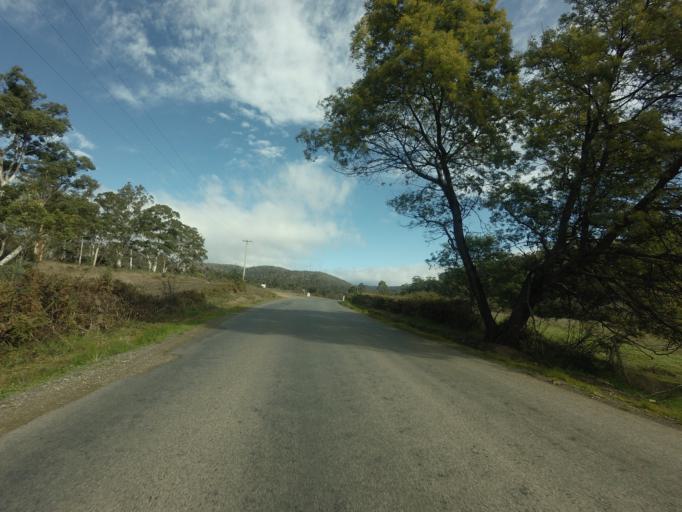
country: AU
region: Tasmania
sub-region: Derwent Valley
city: New Norfolk
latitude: -42.7813
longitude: 147.0076
